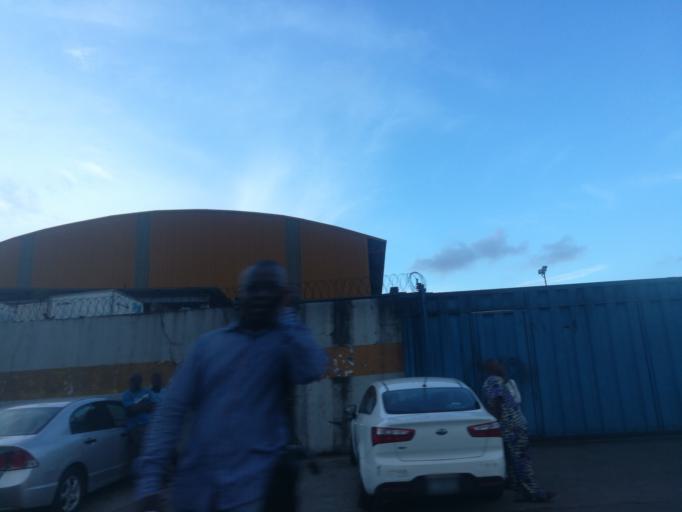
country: NG
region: Lagos
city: Somolu
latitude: 6.5530
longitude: 3.3761
